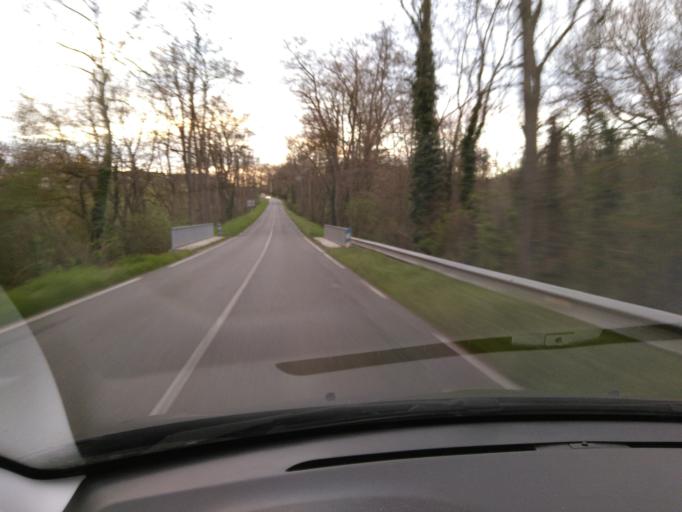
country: FR
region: Midi-Pyrenees
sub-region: Departement de la Haute-Garonne
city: Brax
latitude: 43.6168
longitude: 1.2580
